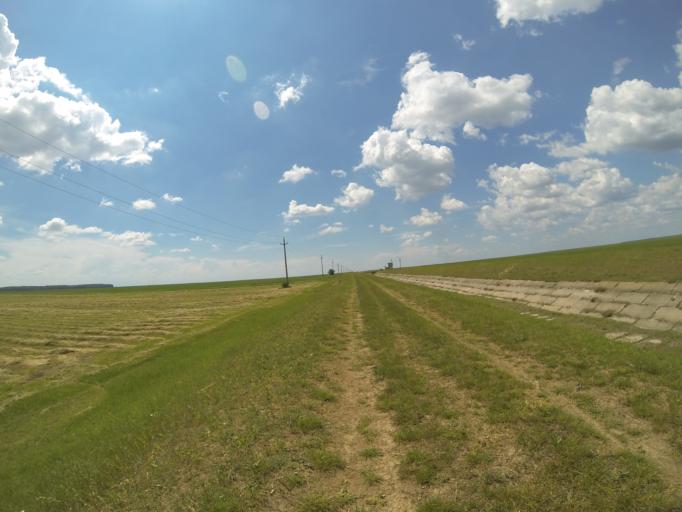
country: RO
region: Dolj
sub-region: Comuna Dranicu
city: Padea
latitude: 44.0116
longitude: 23.8366
